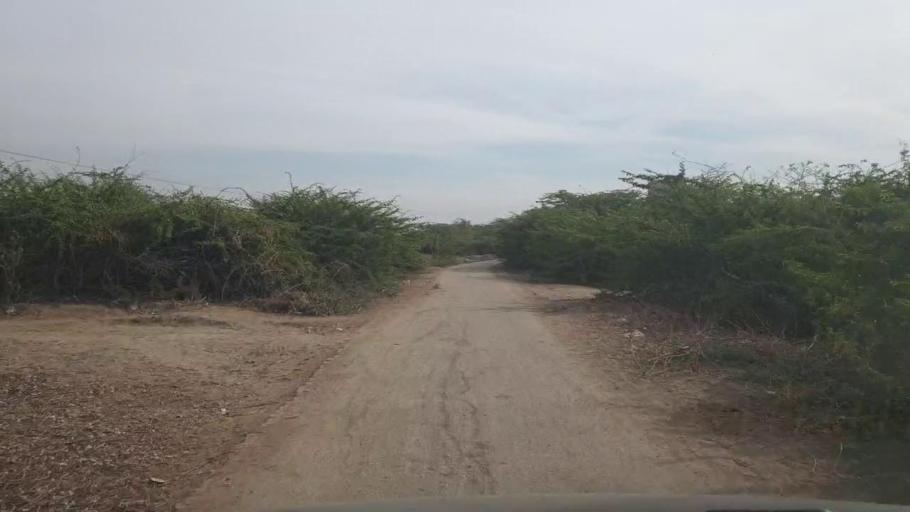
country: PK
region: Sindh
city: Kunri
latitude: 25.2864
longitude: 69.5991
